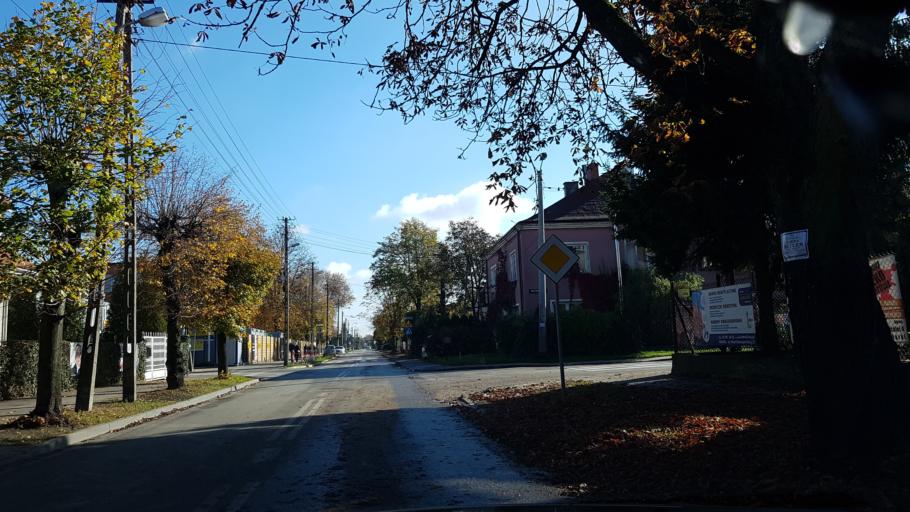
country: PL
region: Masovian Voivodeship
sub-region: Powiat wolominski
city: Marki
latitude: 52.3174
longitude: 21.1021
